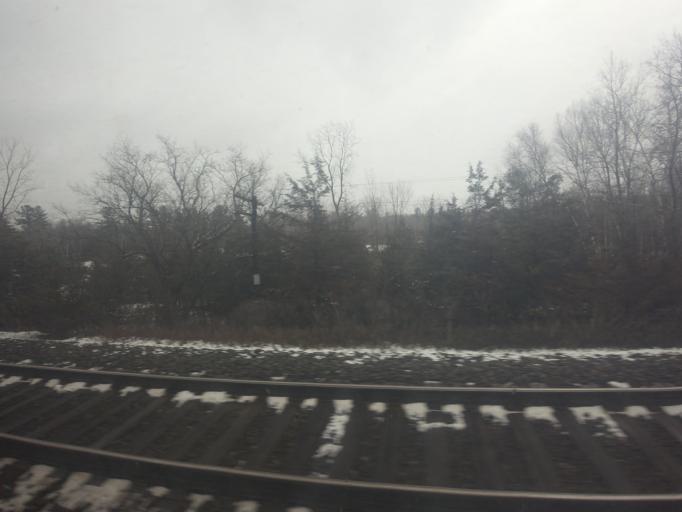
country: CA
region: Ontario
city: Quinte West
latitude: 44.1069
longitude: -77.6059
